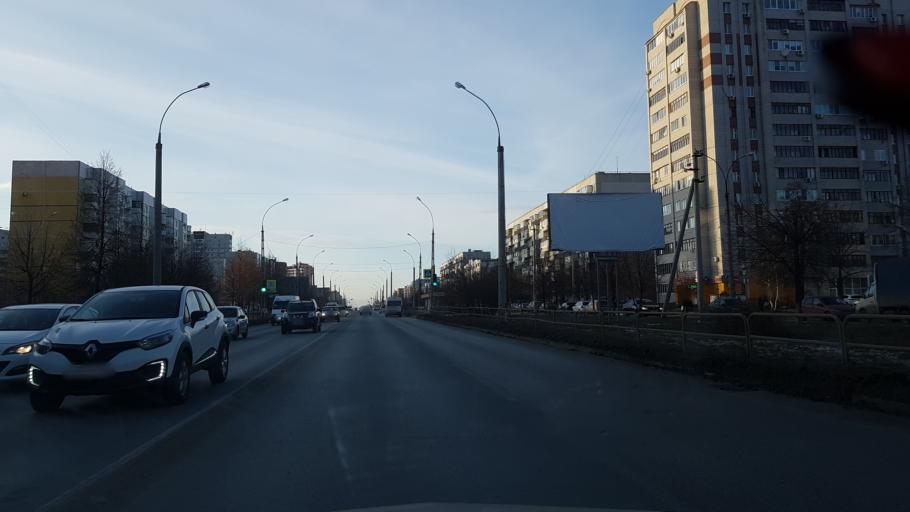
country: RU
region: Samara
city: Tol'yatti
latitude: 53.5405
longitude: 49.3531
